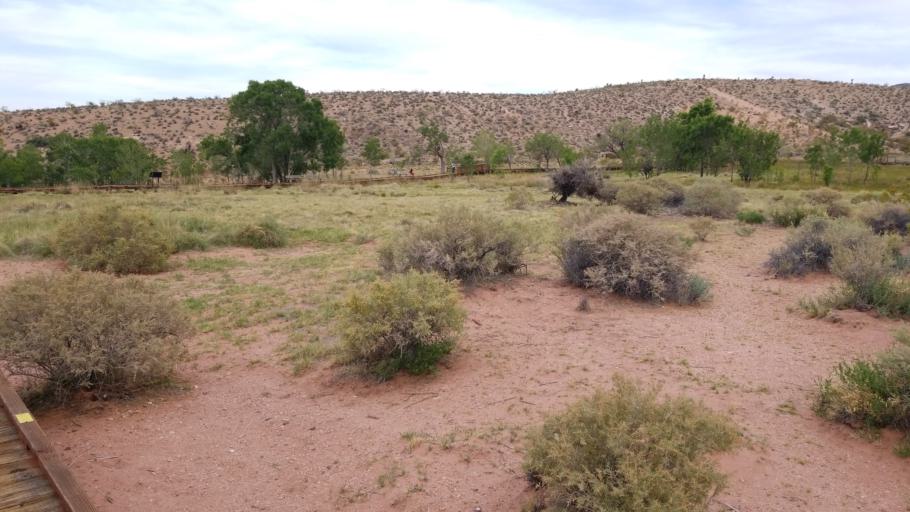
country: US
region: Nevada
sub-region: Clark County
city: Summerlin South
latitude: 36.1461
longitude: -115.4206
